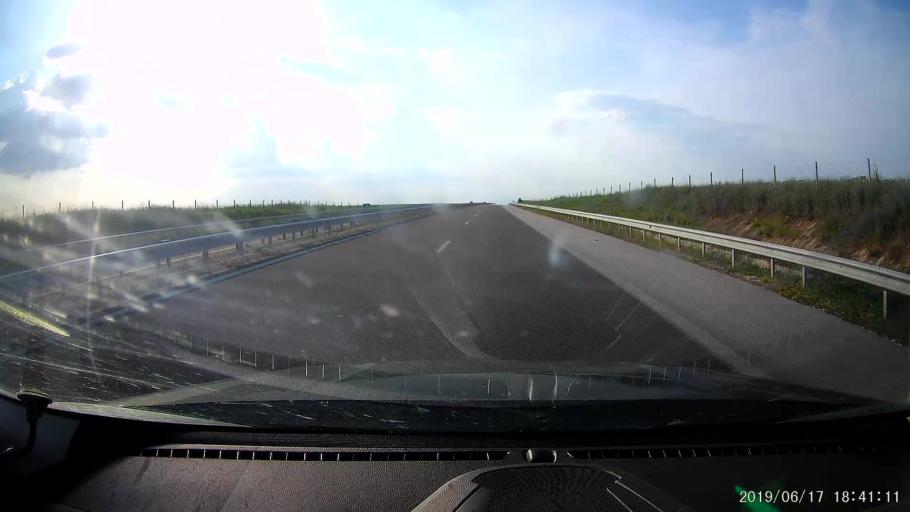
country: BG
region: Stara Zagora
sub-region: Obshtina Chirpan
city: Chirpan
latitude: 42.1674
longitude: 25.2605
